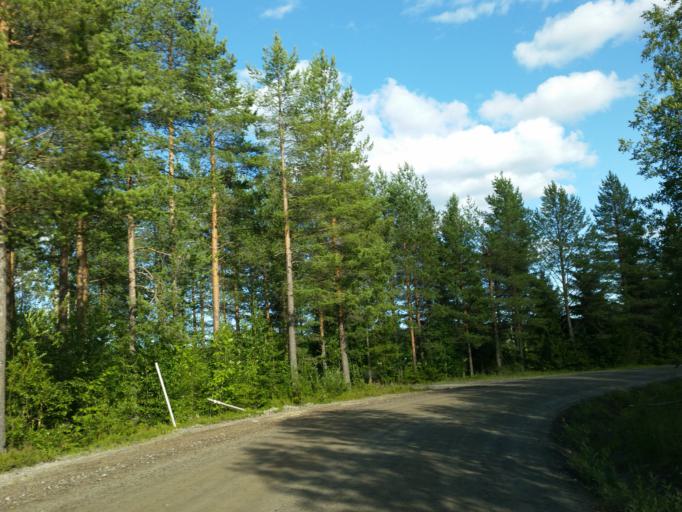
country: SE
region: Vaesterbotten
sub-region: Robertsfors Kommun
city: Robertsfors
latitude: 64.1387
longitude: 20.8786
